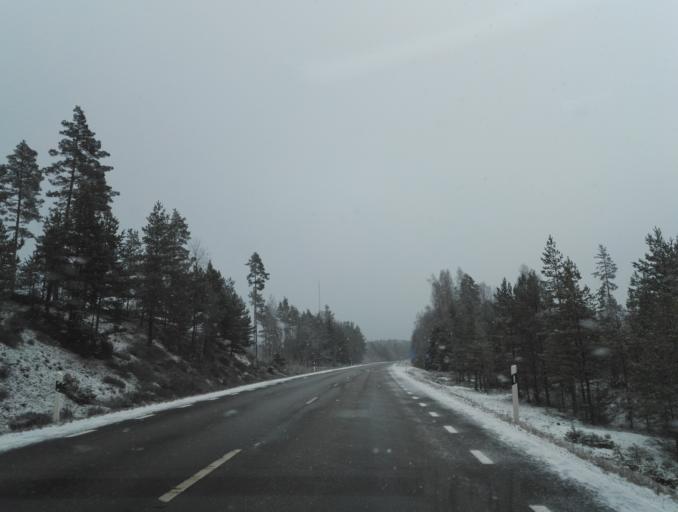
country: SE
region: Kronoberg
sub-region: Uppvidinge Kommun
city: Lenhovda
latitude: 56.9257
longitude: 15.3555
